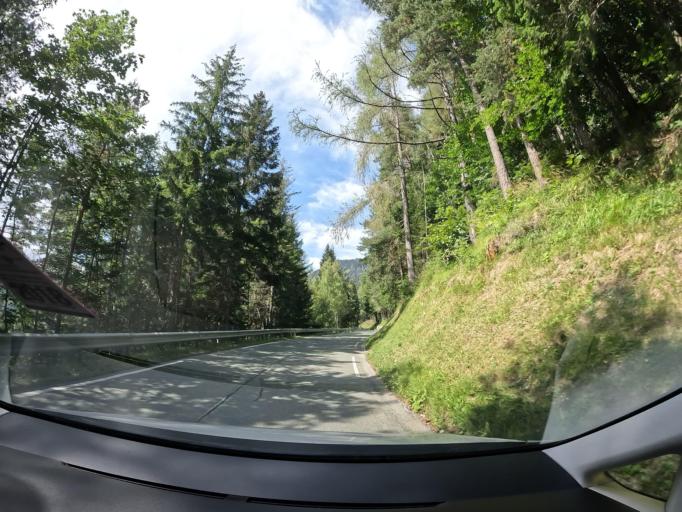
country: AT
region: Carinthia
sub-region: Politischer Bezirk Feldkirchen
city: Glanegg
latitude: 46.7369
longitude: 14.2111
